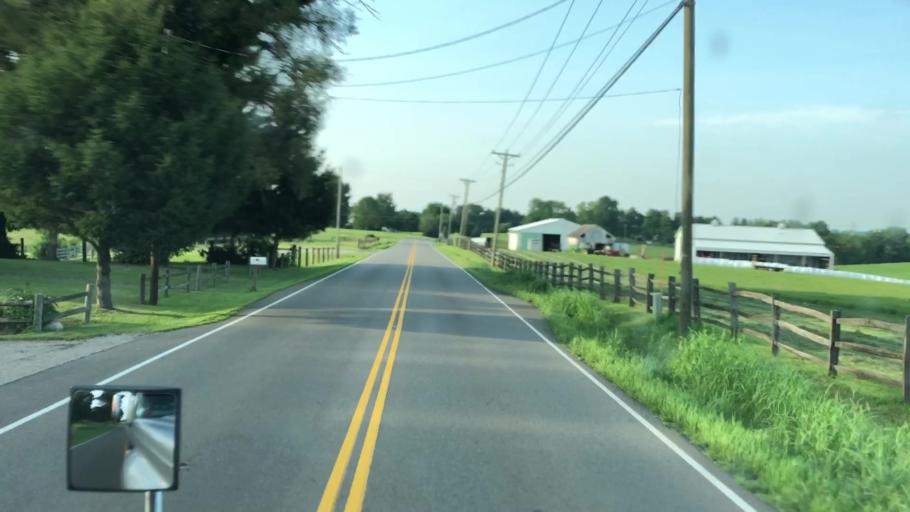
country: US
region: Ohio
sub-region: Muskingum County
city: Pleasant Grove
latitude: 39.9682
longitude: -81.9552
